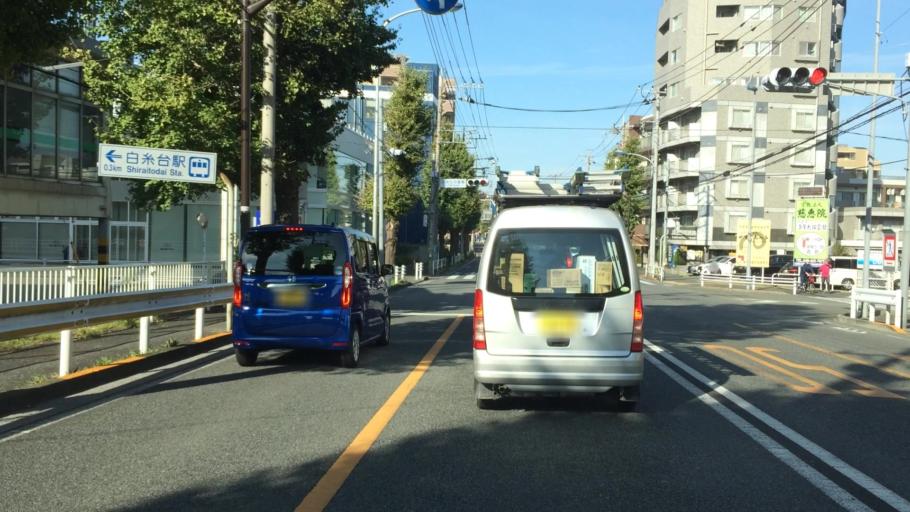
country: JP
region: Tokyo
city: Chofugaoka
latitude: 35.6693
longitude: 139.5104
